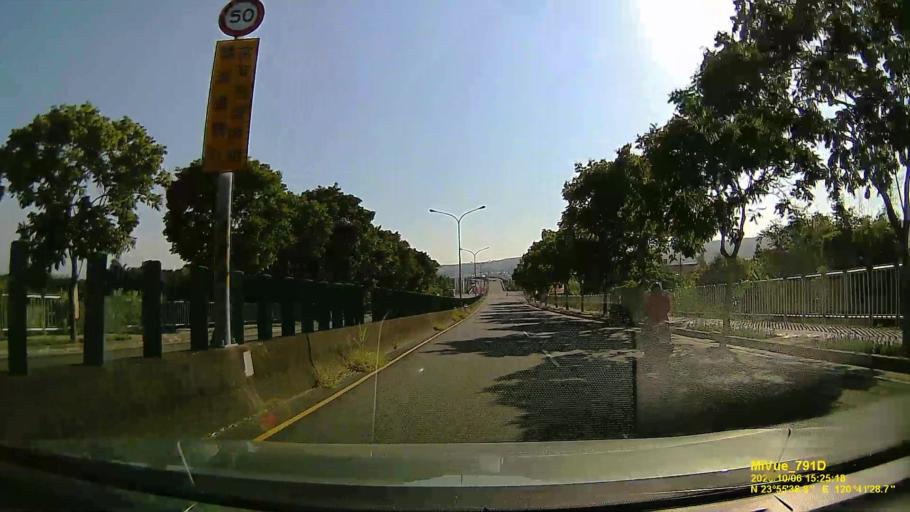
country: TW
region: Taiwan
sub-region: Nantou
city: Nantou
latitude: 23.9274
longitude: 120.6913
